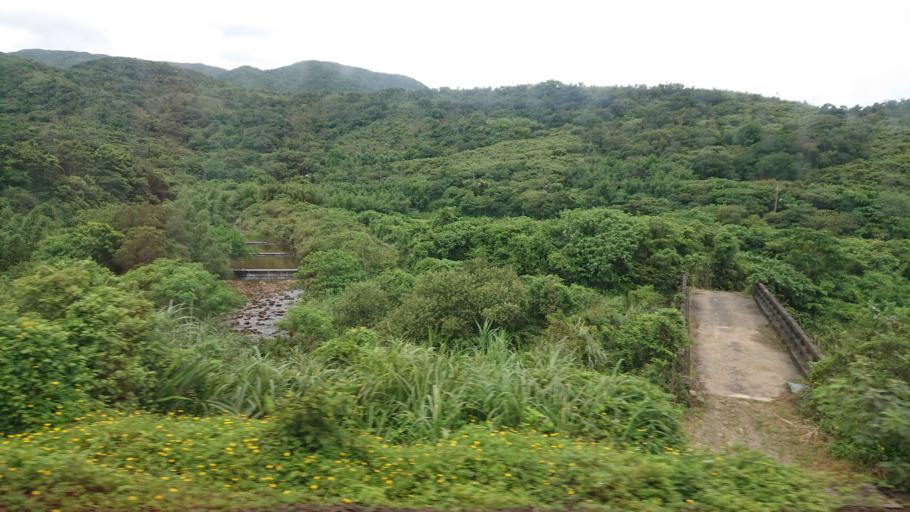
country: TW
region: Taiwan
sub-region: Keelung
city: Keelung
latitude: 25.0101
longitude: 121.9540
